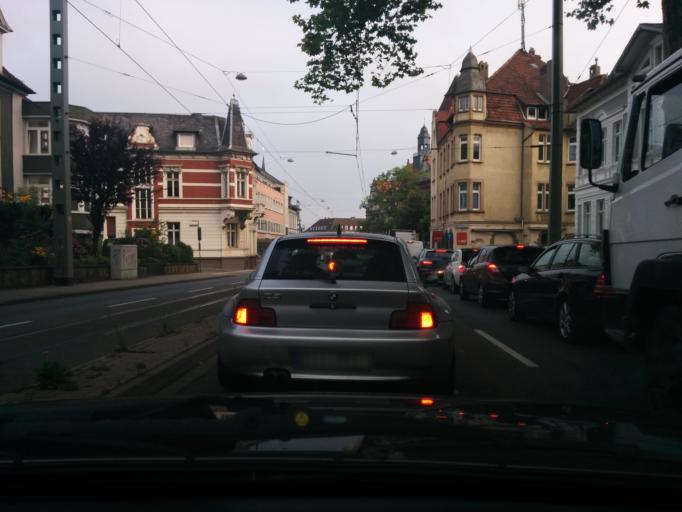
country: DE
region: North Rhine-Westphalia
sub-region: Regierungsbezirk Detmold
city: Bielefeld
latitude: 52.0142
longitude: 8.5338
